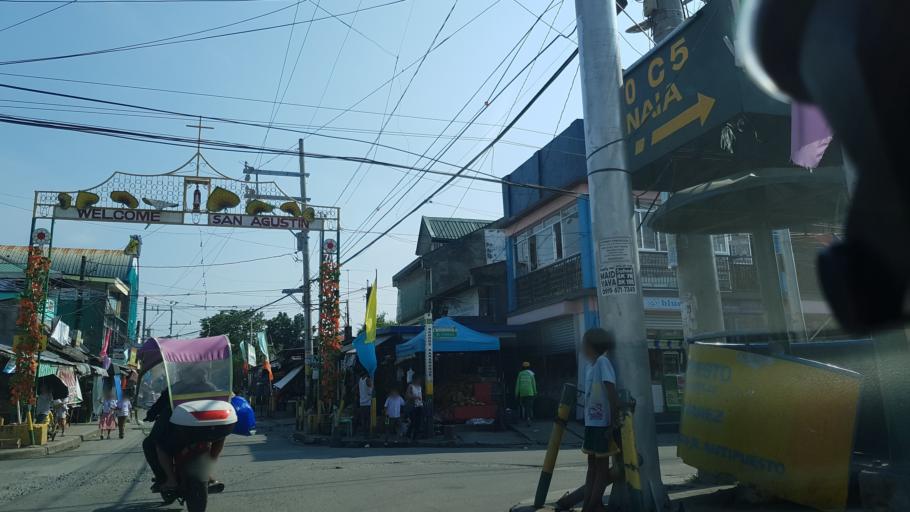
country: PH
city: Sambayanihan People's Village
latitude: 14.4921
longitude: 121.0147
